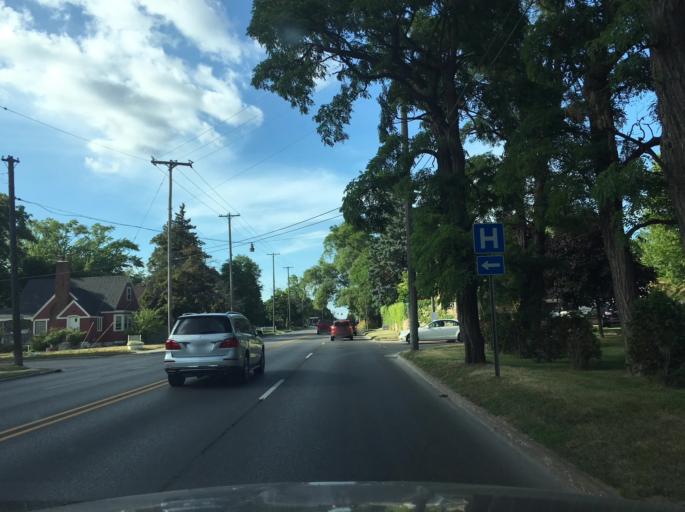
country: US
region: Michigan
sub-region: Grand Traverse County
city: Traverse City
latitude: 44.7613
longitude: -85.6346
